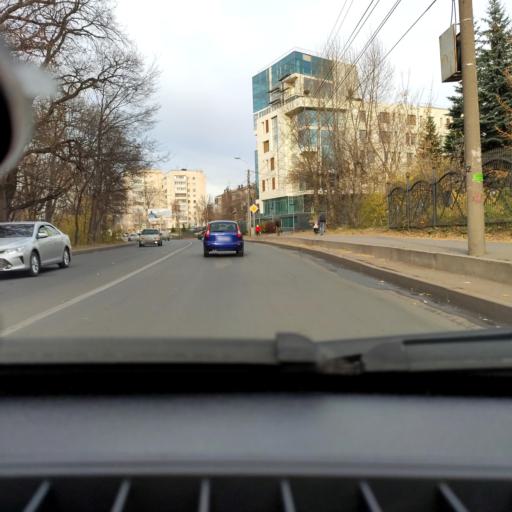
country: RU
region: Bashkortostan
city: Ufa
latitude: 54.7755
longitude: 56.0204
